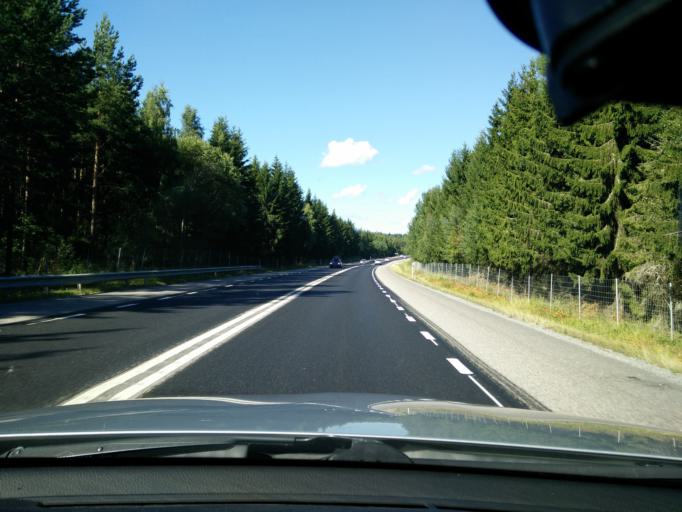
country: SE
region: Stockholm
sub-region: Taby Kommun
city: Taby
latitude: 59.4546
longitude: 18.1482
